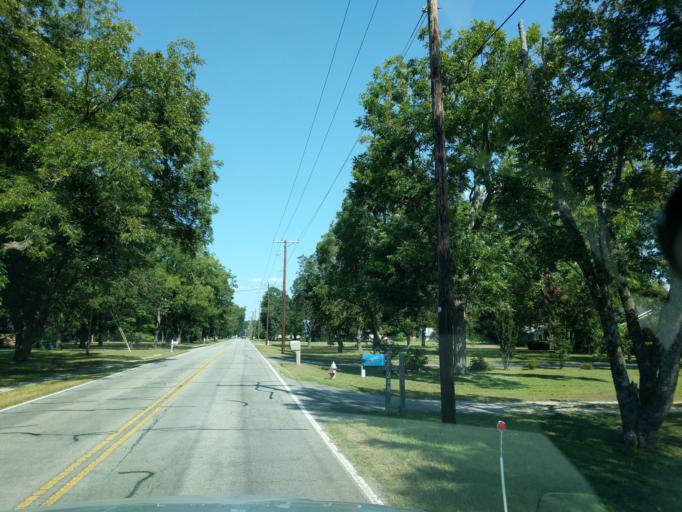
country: US
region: South Carolina
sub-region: Lexington County
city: Batesburg-Leesville
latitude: 33.9156
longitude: -81.5432
